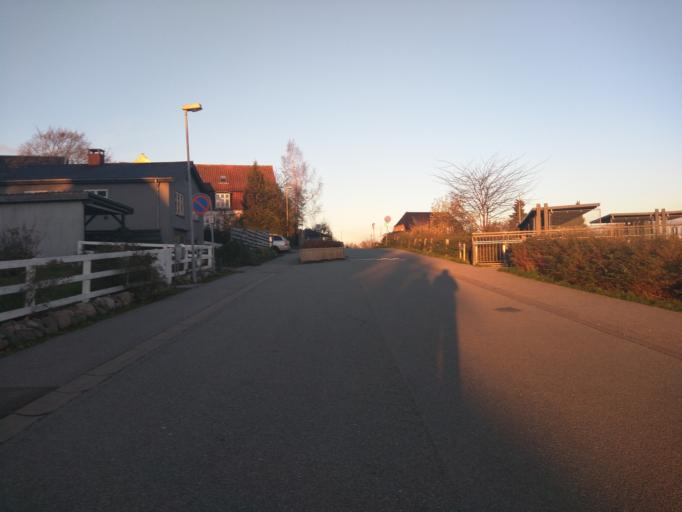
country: DK
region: Central Jutland
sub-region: Skanderborg Kommune
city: Horning
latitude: 56.0826
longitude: 10.0379
